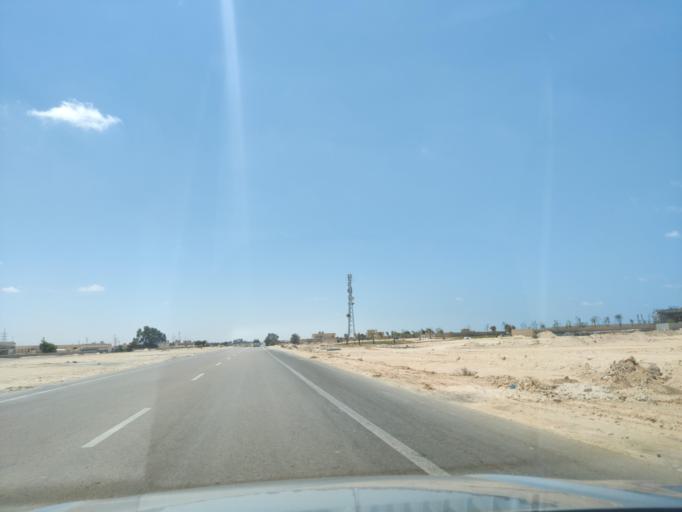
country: EG
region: Muhafazat Matruh
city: Al `Alamayn
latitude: 31.0698
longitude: 28.1392
